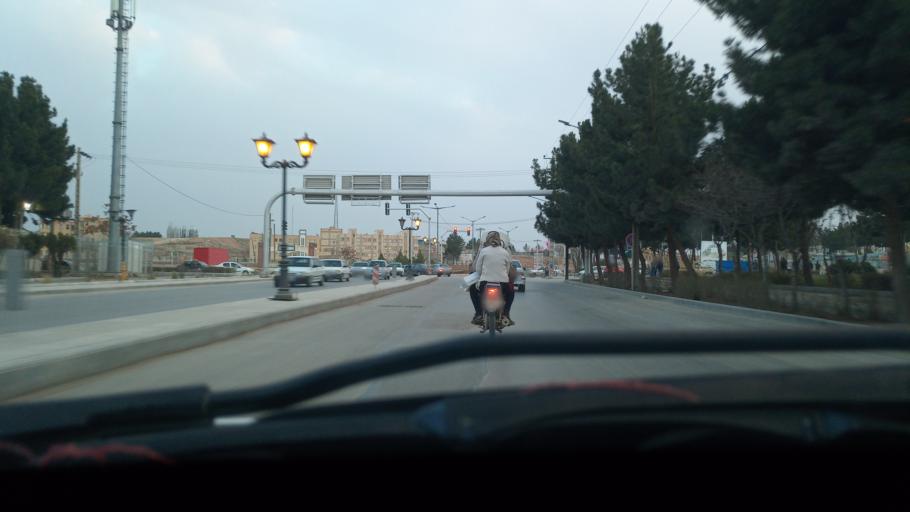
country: IR
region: Khorasan-e Shomali
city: Bojnurd
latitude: 37.4609
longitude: 57.3324
